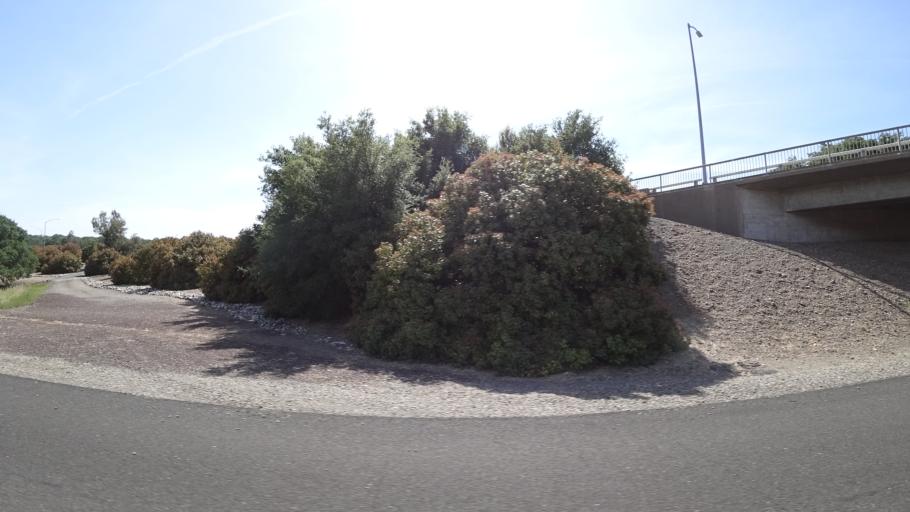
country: US
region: California
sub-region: Tehama County
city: Red Bluff
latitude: 40.2032
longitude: -122.2439
